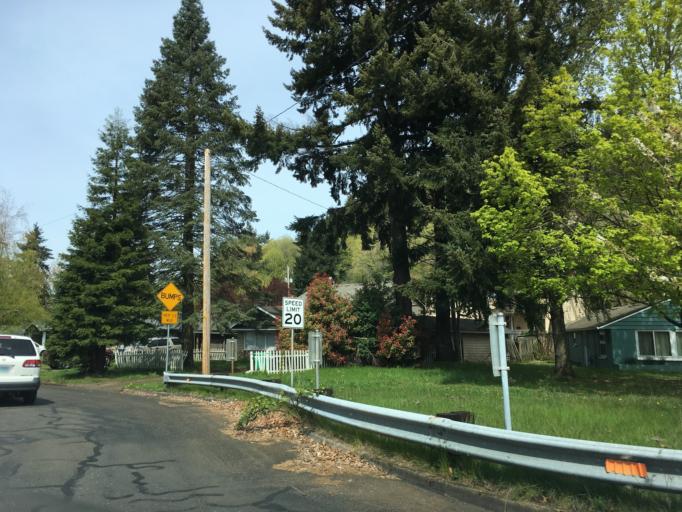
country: US
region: Oregon
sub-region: Multnomah County
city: Lents
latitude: 45.5410
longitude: -122.5697
